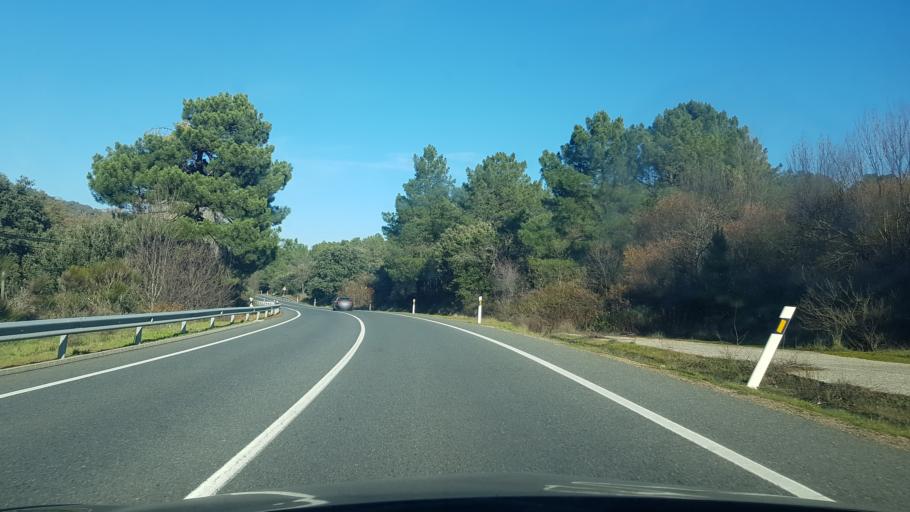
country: ES
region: Madrid
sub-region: Provincia de Madrid
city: Rozas de Puerto Real
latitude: 40.3365
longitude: -4.4627
